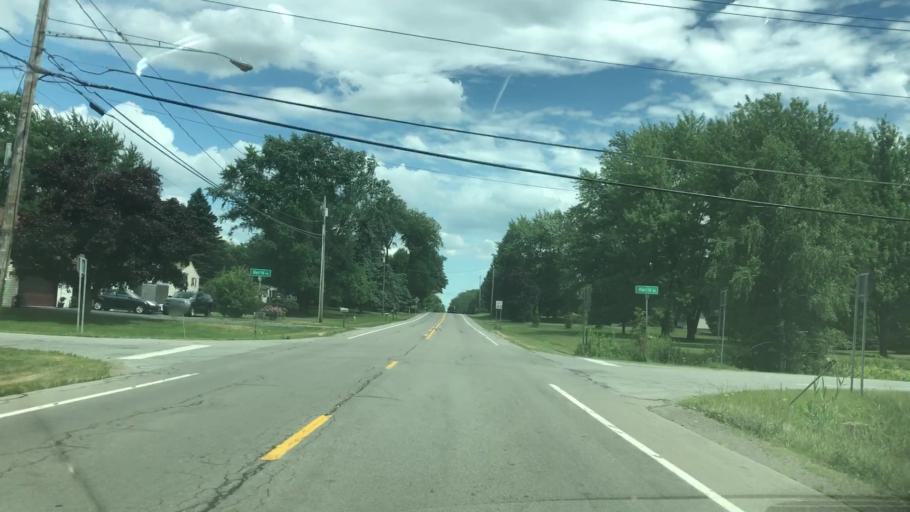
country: US
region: New York
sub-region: Monroe County
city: Webster
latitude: 43.1597
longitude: -77.4126
